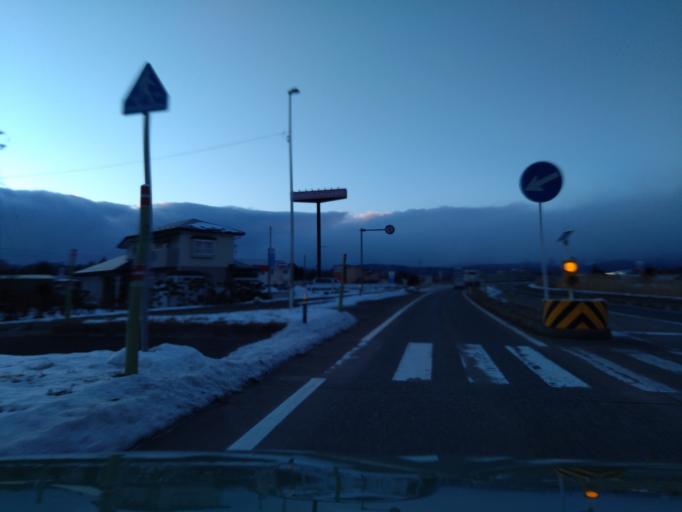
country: JP
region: Iwate
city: Shizukuishi
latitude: 39.6924
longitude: 140.9831
